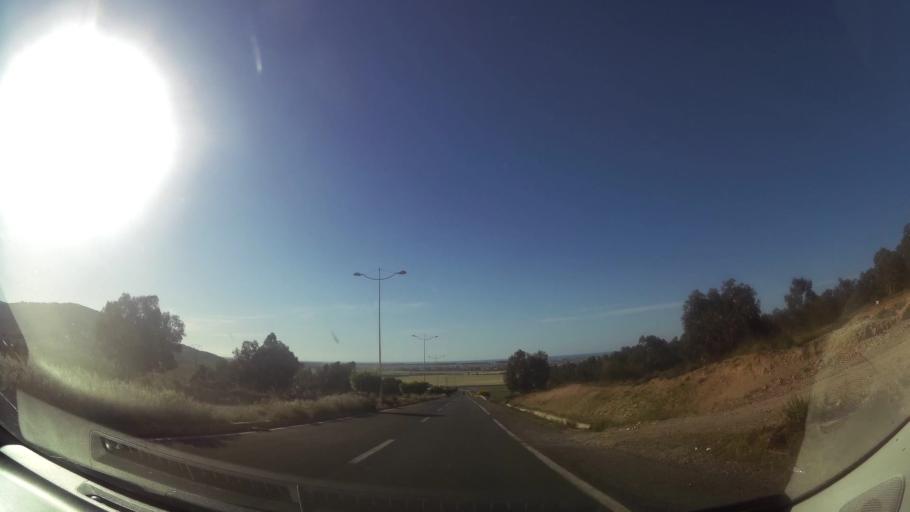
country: MA
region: Oriental
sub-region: Berkane-Taourirt
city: Madagh
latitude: 35.0595
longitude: -2.2225
